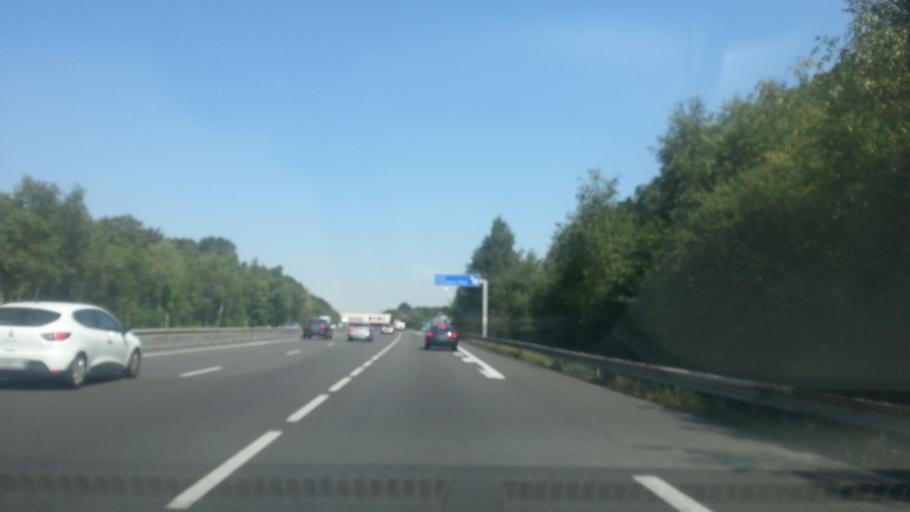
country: FR
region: Centre
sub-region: Departement du Loiret
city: Gidy
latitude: 47.9720
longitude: 1.8585
